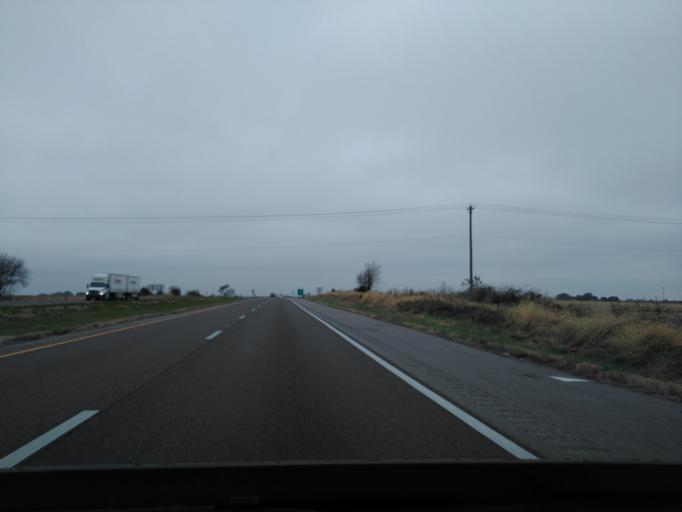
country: US
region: Illinois
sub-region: Madison County
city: Saint Jacob
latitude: 38.7638
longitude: -89.7813
